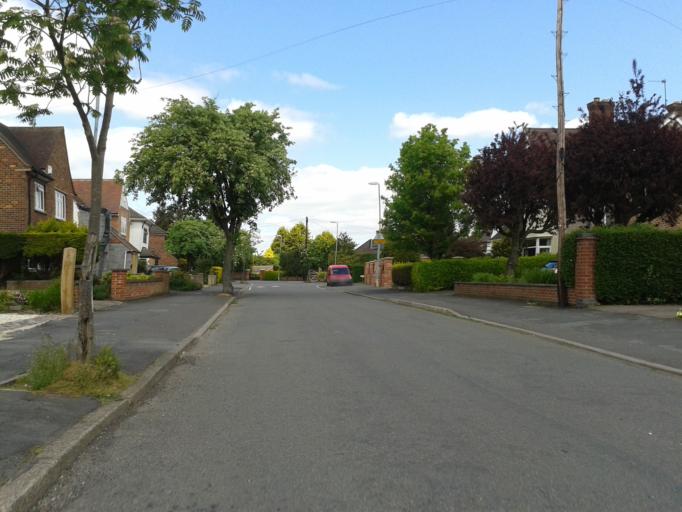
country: GB
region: England
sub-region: Leicestershire
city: Hinckley
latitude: 52.5478
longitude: -1.3542
